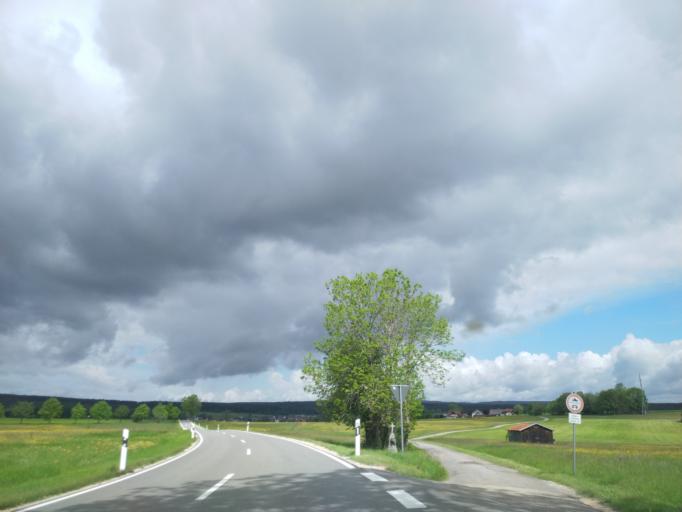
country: DE
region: Baden-Wuerttemberg
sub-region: Freiburg Region
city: Loffingen
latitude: 47.8843
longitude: 8.3046
